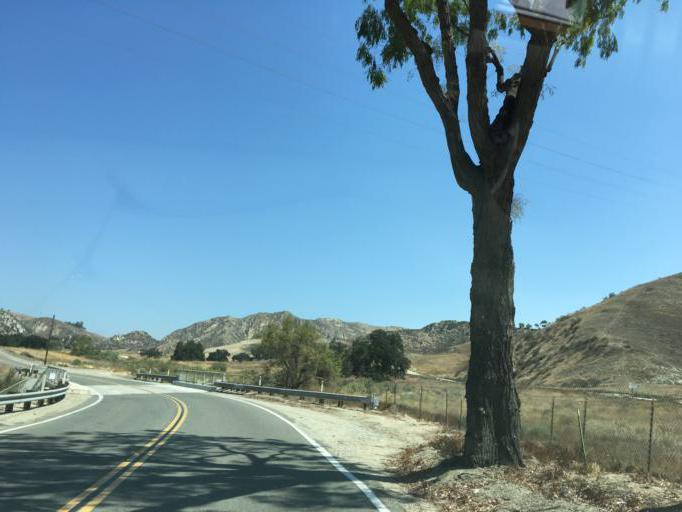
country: US
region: California
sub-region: Los Angeles County
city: Val Verde
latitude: 34.4235
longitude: -118.6570
